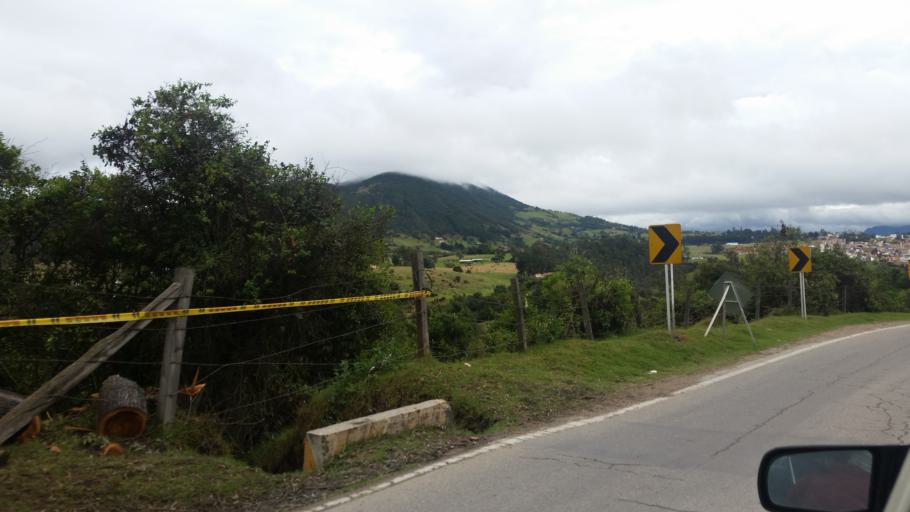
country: CO
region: Cundinamarca
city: La Calera
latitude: 4.7073
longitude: -73.9752
